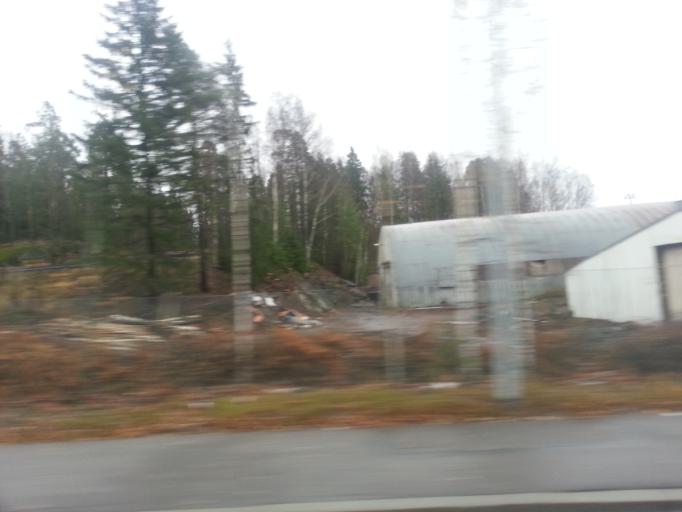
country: FI
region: Uusimaa
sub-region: Helsinki
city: Vantaa
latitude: 60.2992
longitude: 24.9514
